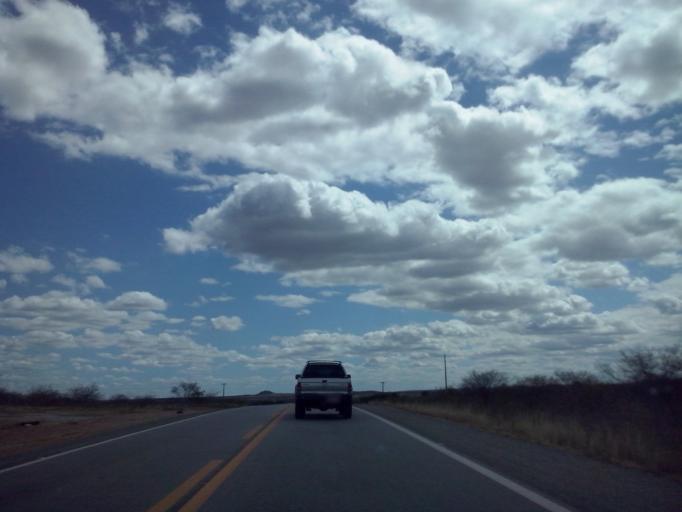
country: BR
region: Paraiba
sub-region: Soledade
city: Soledade
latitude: -7.0387
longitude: -36.4200
